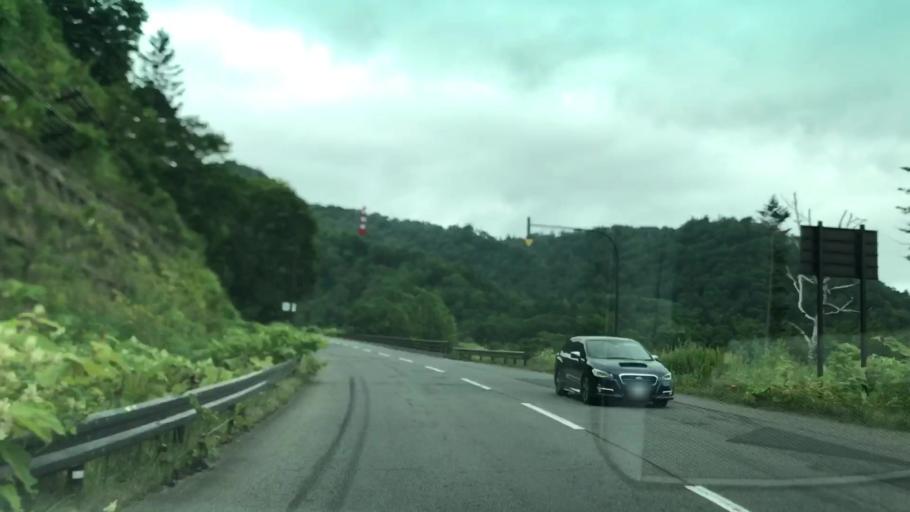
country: JP
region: Hokkaido
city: Otaru
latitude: 42.9896
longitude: 140.8738
